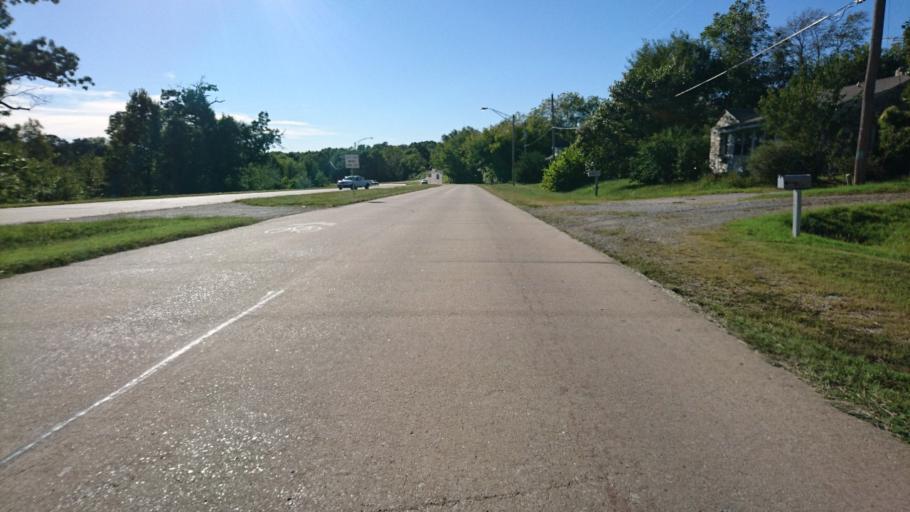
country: US
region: Missouri
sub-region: Jasper County
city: Carthage
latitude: 37.1766
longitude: -94.3413
